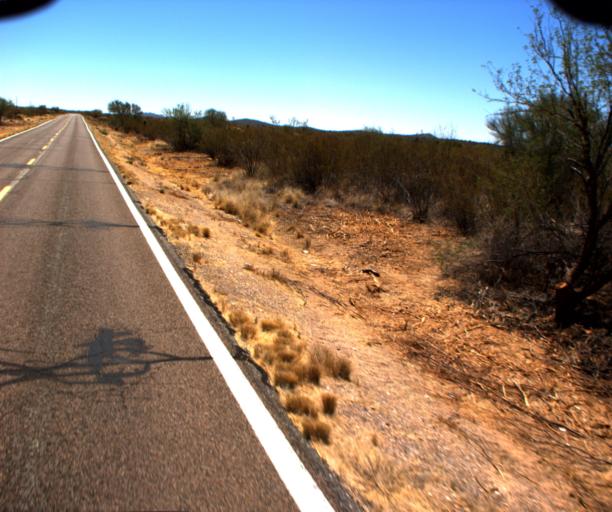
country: US
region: Arizona
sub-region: Pima County
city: Ajo
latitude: 32.2183
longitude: -112.6529
